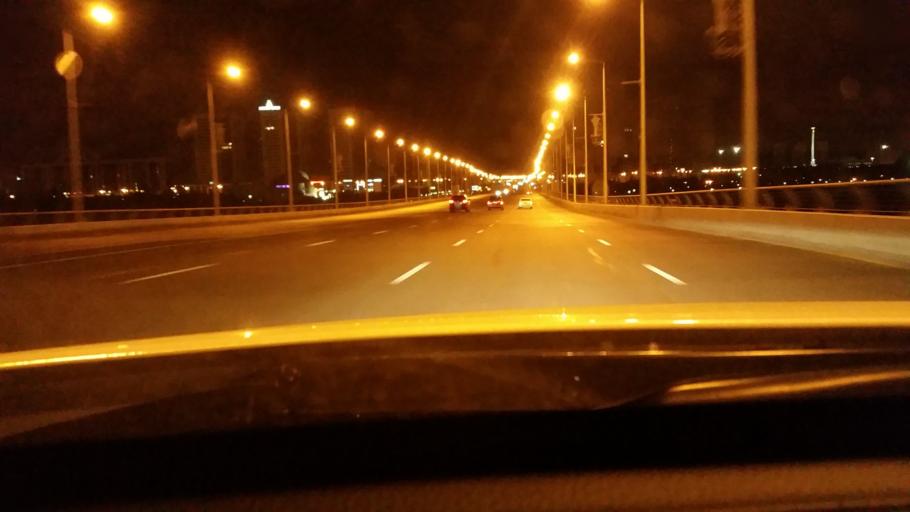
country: KZ
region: Astana Qalasy
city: Astana
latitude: 51.1308
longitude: 71.4490
